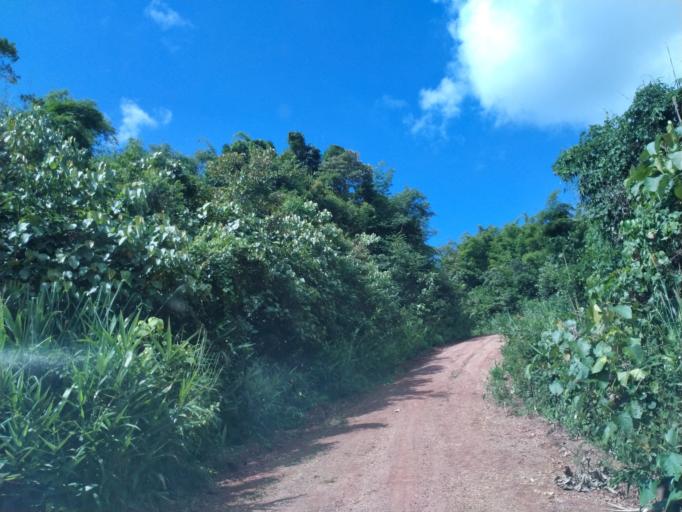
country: LA
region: Vientiane
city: Muang Phon-Hong
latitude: 18.6445
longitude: 102.9006
